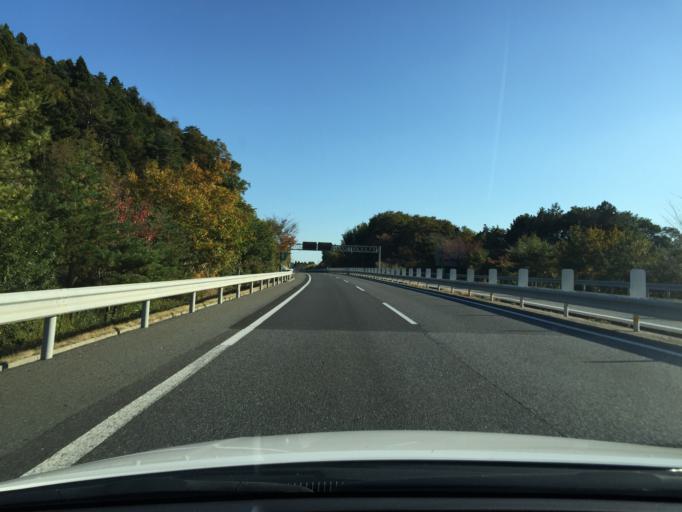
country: JP
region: Fukushima
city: Iwaki
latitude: 37.0457
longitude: 140.8076
